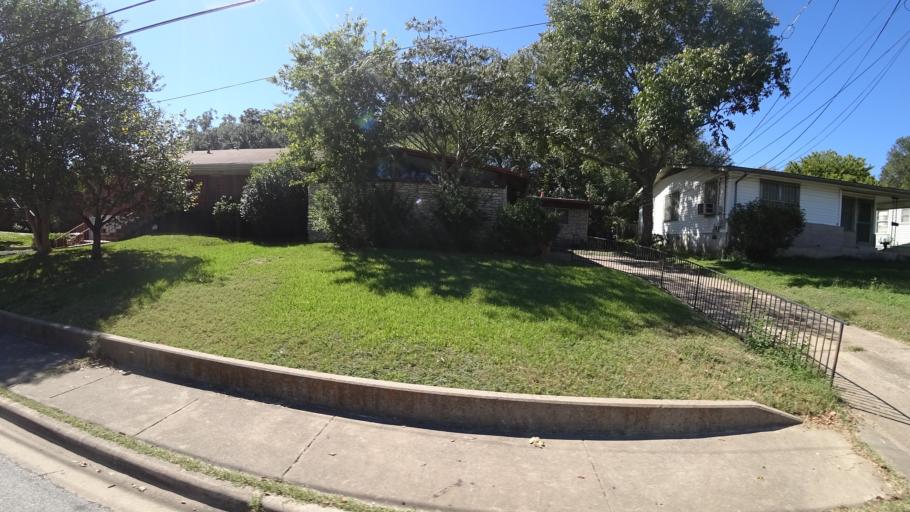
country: US
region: Texas
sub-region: Travis County
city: Austin
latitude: 30.2816
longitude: -97.7165
